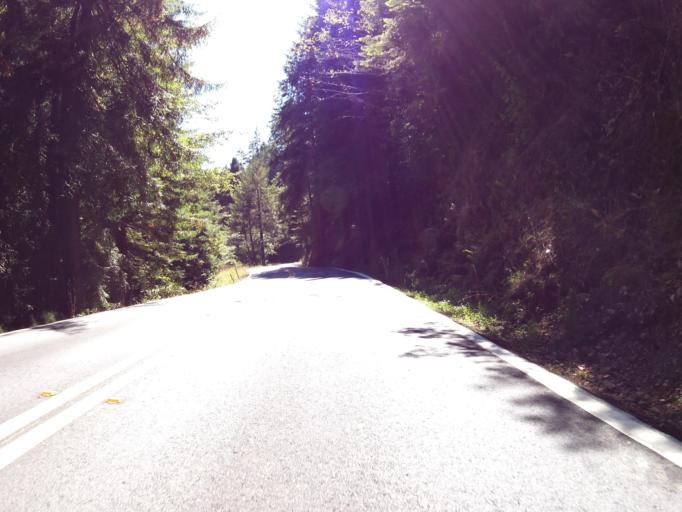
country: US
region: California
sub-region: Mendocino County
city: Fort Bragg
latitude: 39.7200
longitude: -123.8015
